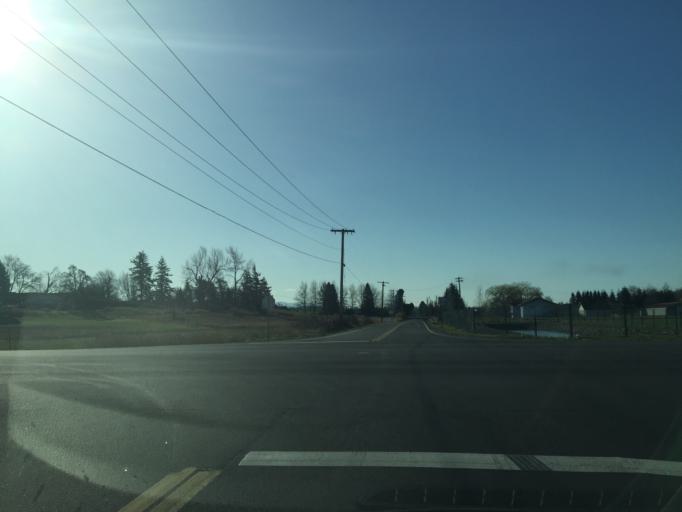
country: US
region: Washington
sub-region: Whatcom County
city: Marietta-Alderwood
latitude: 48.8336
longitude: -122.5188
